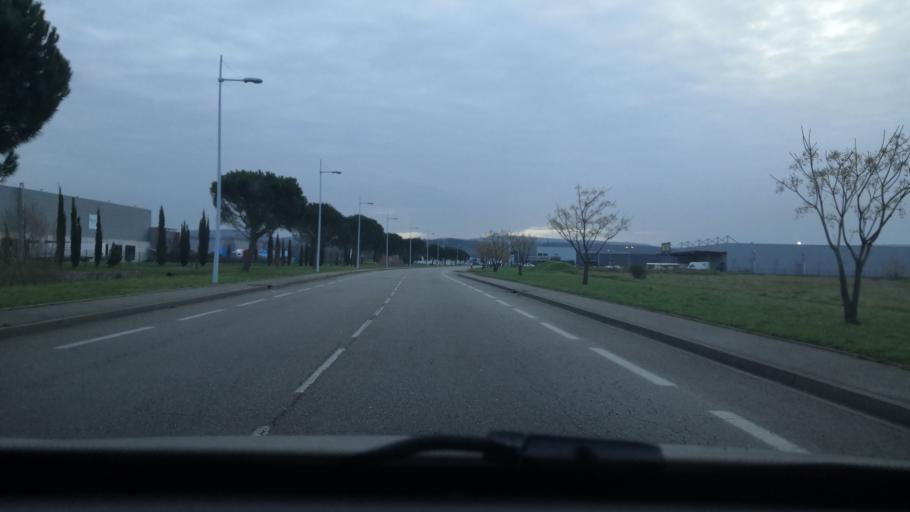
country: FR
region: Rhone-Alpes
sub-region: Departement de la Drome
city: Montelimar
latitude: 44.5271
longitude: 4.7374
